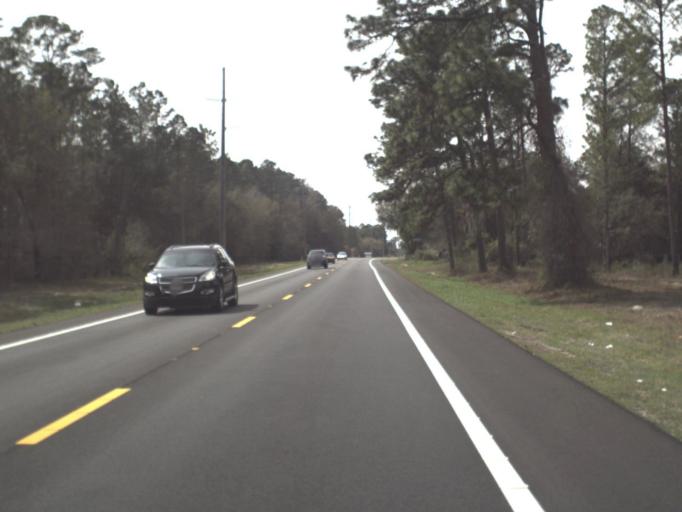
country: US
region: Florida
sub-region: Gadsden County
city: Midway
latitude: 30.4407
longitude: -84.4506
